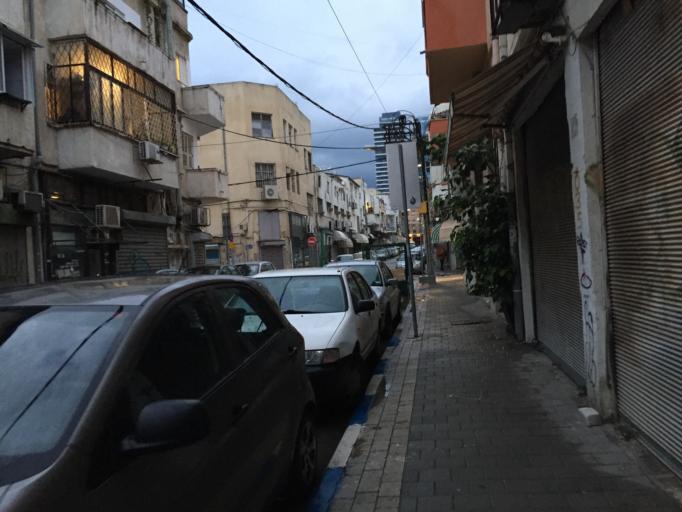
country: IL
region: Tel Aviv
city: Yafo
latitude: 32.0584
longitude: 34.7699
